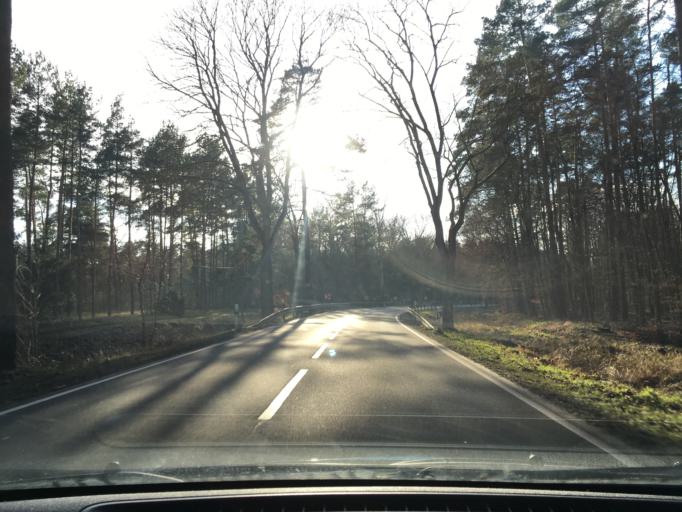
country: DE
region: Saxony-Anhalt
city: Seehausen
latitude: 52.8857
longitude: 11.6550
